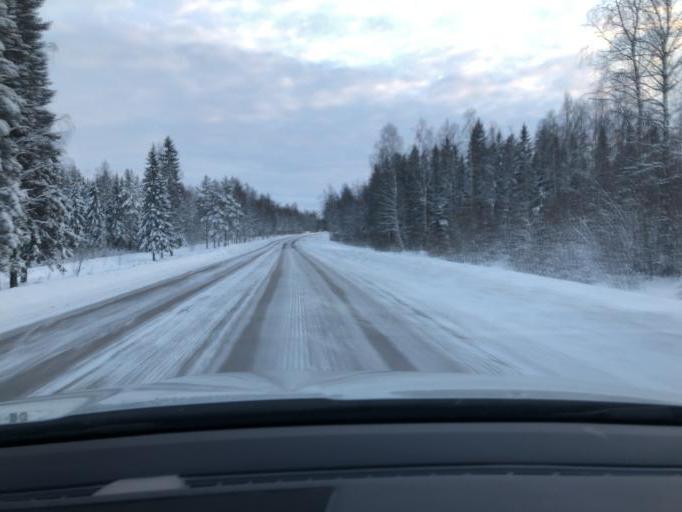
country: SE
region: Norrbotten
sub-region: Lulea Kommun
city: Bergnaset
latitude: 65.6224
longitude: 22.1253
